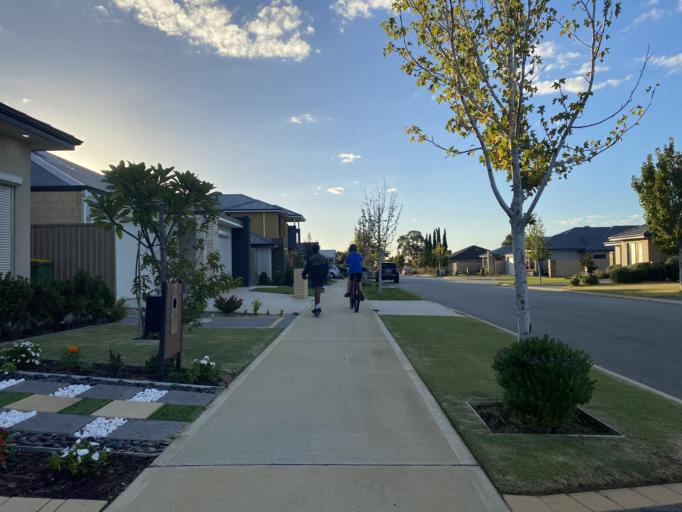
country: AU
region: Western Australia
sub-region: Kalamunda
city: Maida Vale
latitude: -31.9708
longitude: 116.0083
